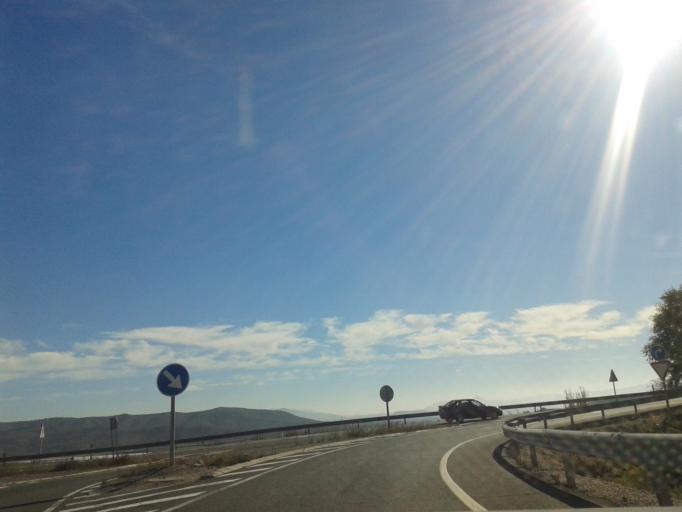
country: ES
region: Castille-La Mancha
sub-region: Provincia de Albacete
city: Caudete
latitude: 38.7325
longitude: -0.9390
